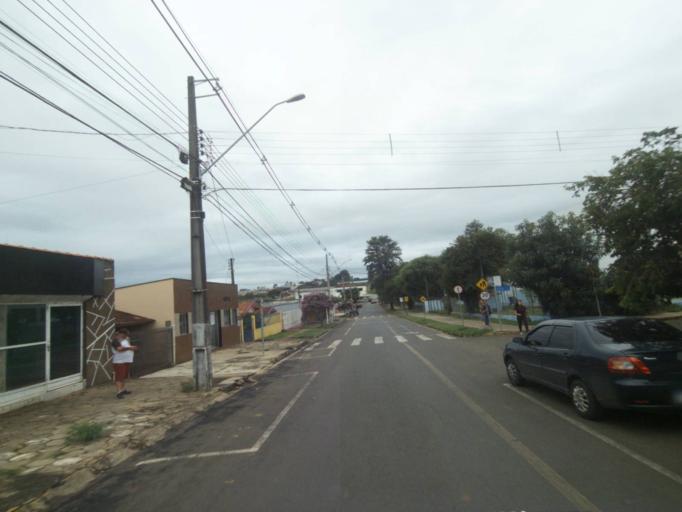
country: BR
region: Parana
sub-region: Telemaco Borba
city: Telemaco Borba
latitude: -24.3331
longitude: -50.6542
